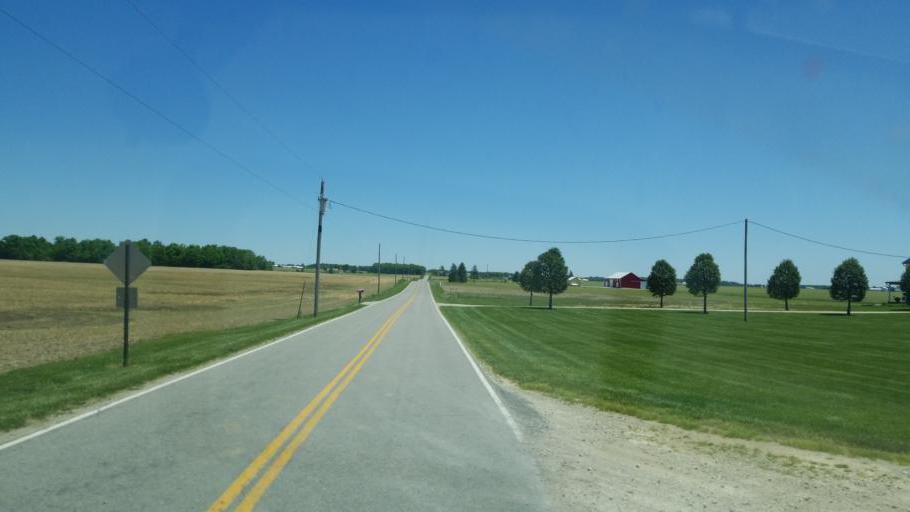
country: US
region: Ohio
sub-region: Darke County
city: Ansonia
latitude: 40.2796
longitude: -84.7264
